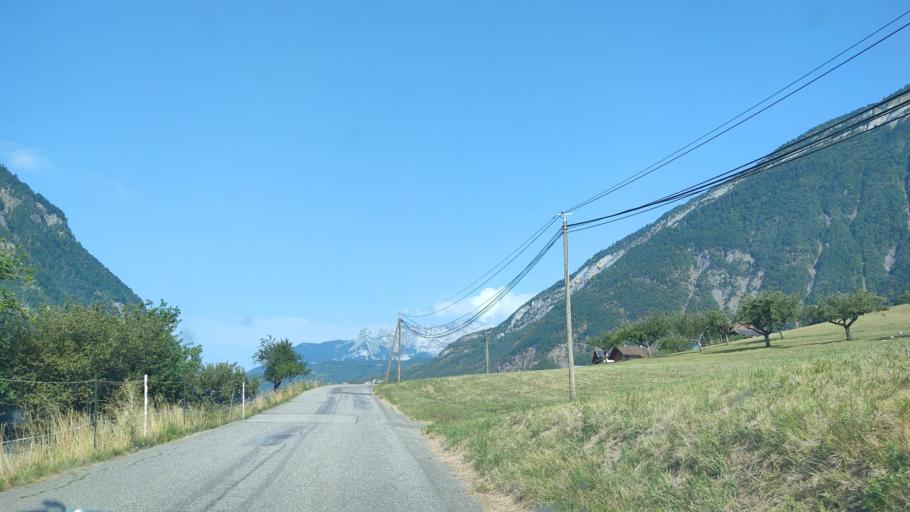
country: FR
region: Rhone-Alpes
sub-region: Departement de la Savoie
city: Ugine
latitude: 45.7619
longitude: 6.4062
